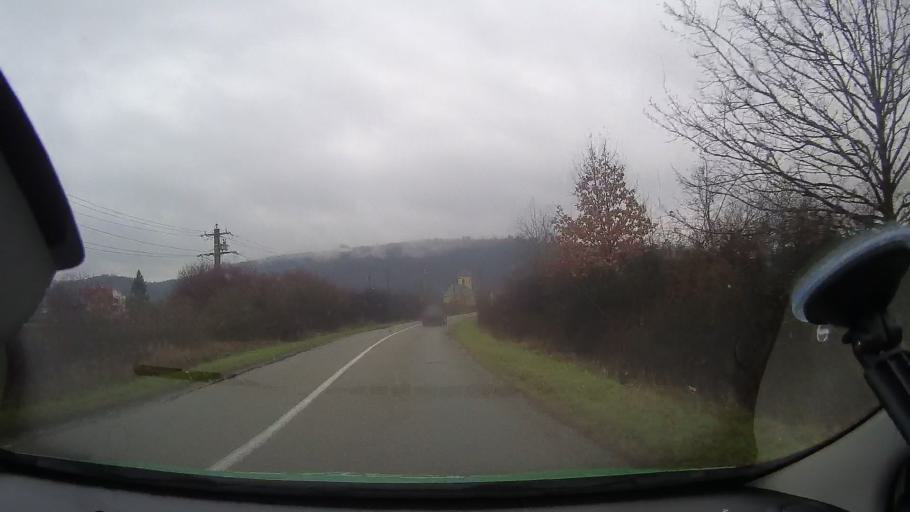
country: RO
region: Arad
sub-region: Comuna Ignesti
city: Ignesti
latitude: 46.3794
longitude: 22.1519
